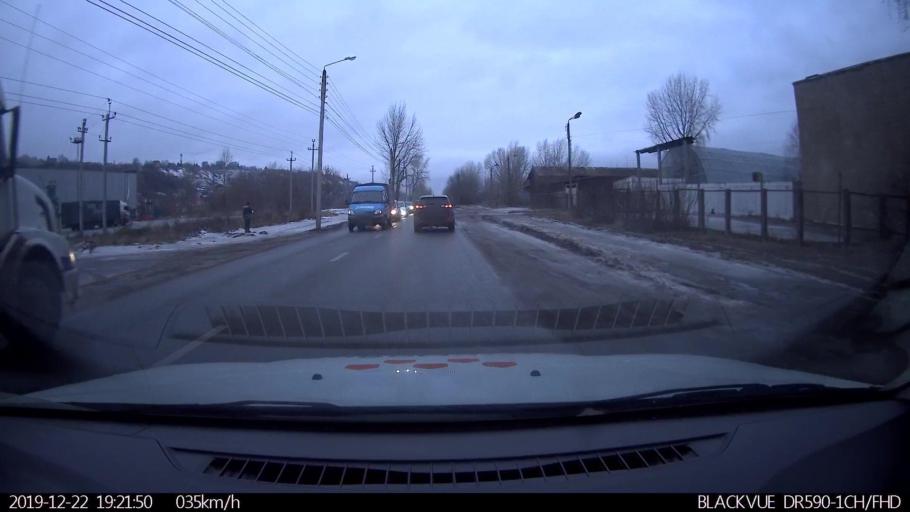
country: RU
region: Nizjnij Novgorod
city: Afonino
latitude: 56.2977
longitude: 44.1060
